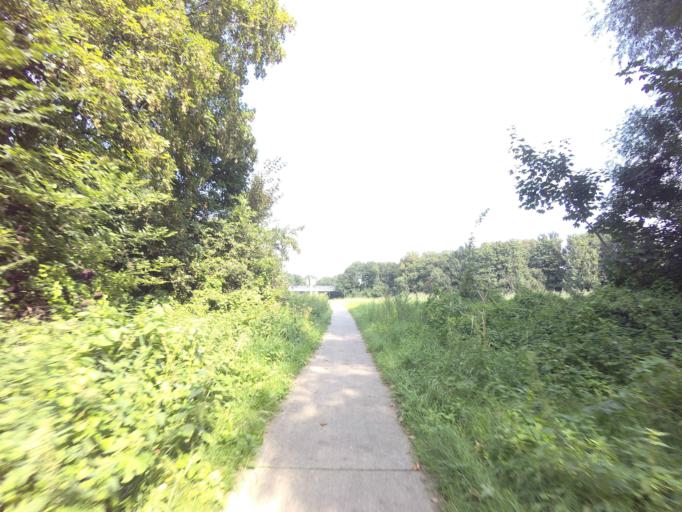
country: NL
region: Flevoland
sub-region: Gemeente Lelystad
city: Lelystad
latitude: 52.5183
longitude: 5.5225
